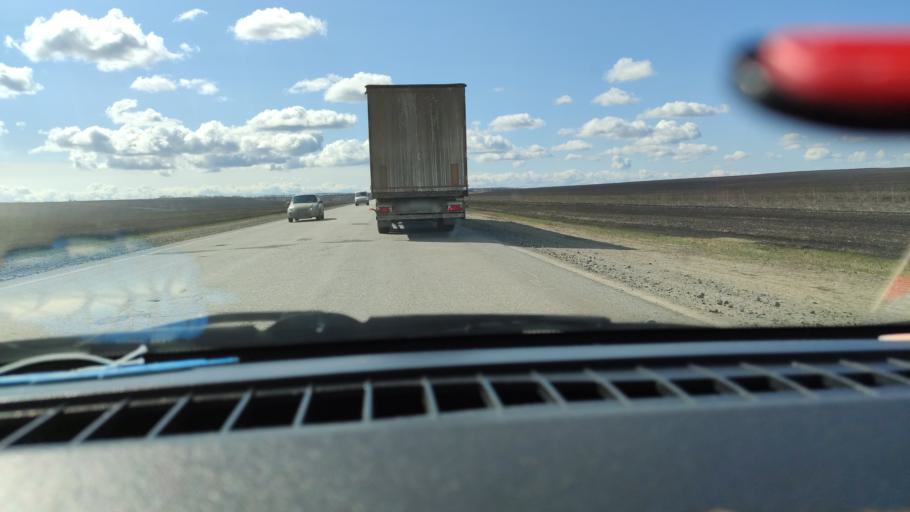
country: RU
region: Samara
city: Varlamovo
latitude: 53.0168
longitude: 48.3329
